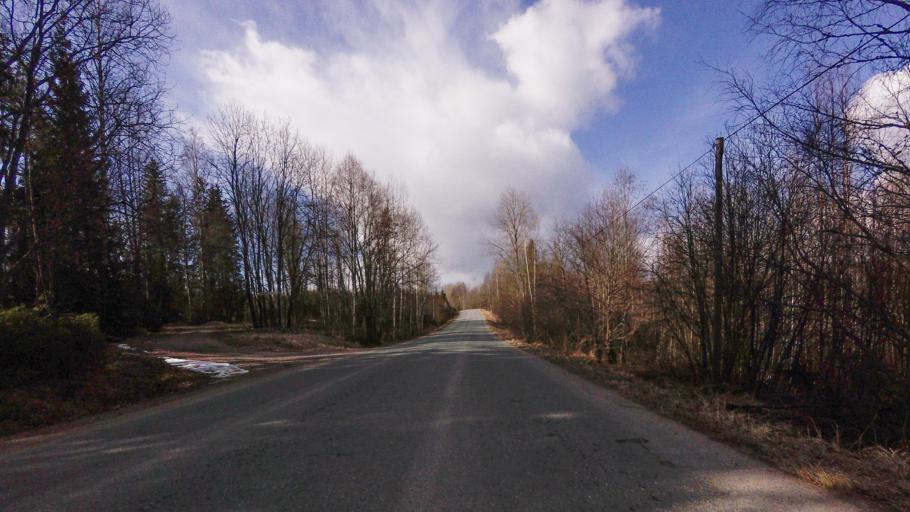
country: FI
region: Varsinais-Suomi
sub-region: Salo
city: Suomusjaervi
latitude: 60.3457
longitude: 23.6775
